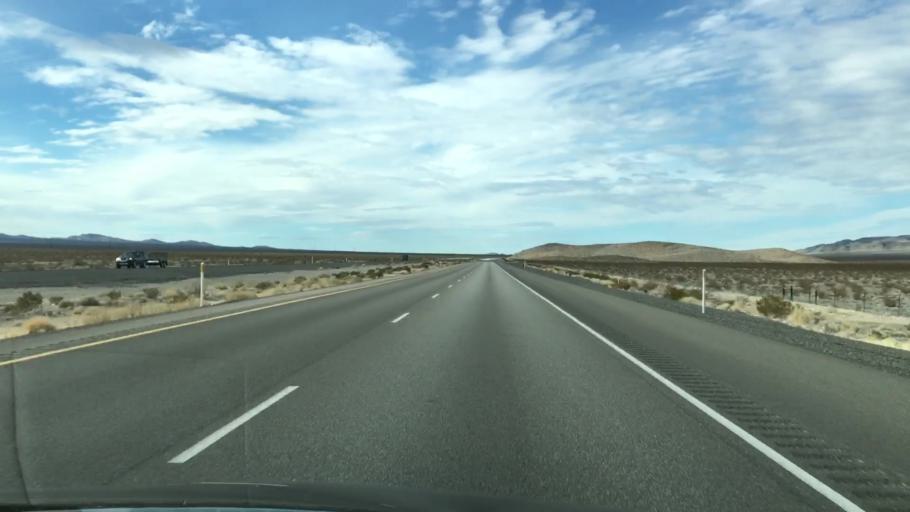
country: US
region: Nevada
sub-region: Nye County
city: Pahrump
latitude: 36.5726
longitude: -115.8600
